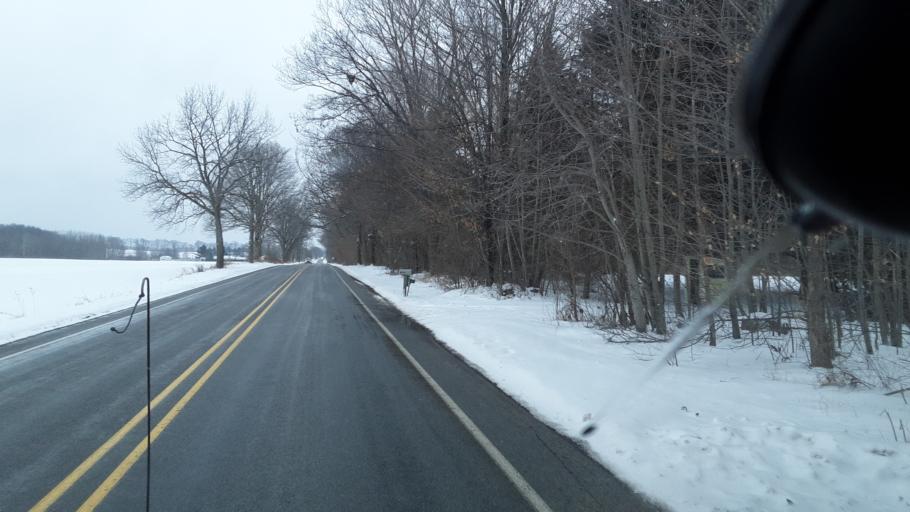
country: US
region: Michigan
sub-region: Ingham County
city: Leslie
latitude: 42.4341
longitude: -84.4137
